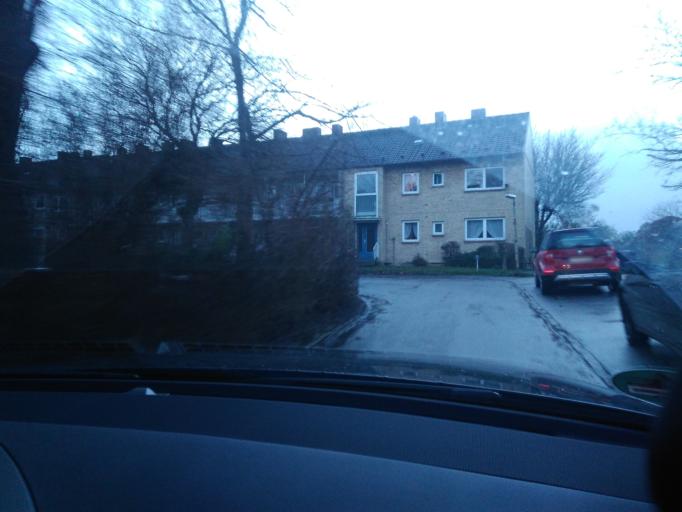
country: DE
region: Schleswig-Holstein
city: Altenholz
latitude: 54.3988
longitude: 10.1601
